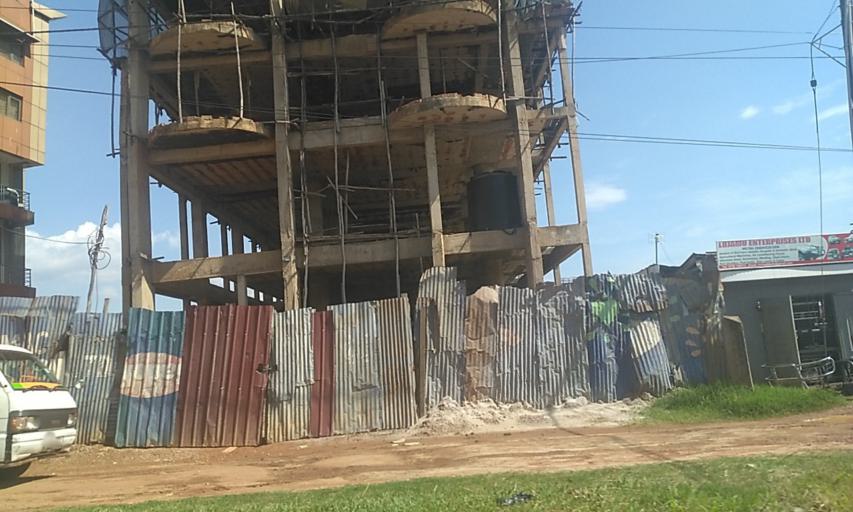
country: UG
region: Central Region
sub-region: Wakiso District
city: Kireka
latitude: 0.3509
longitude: 32.6563
